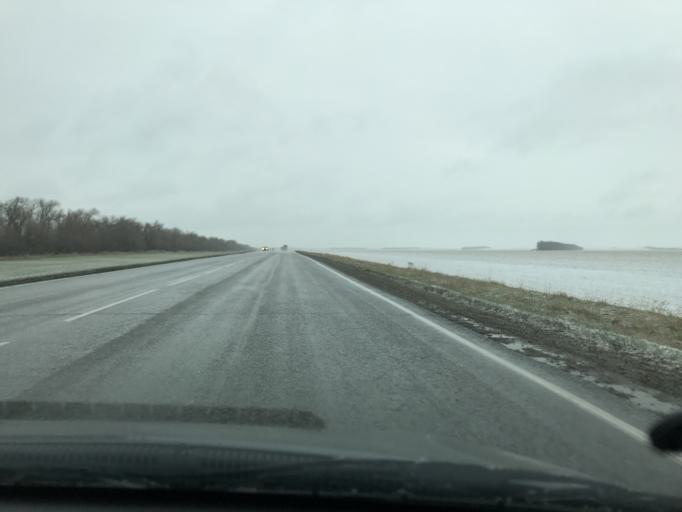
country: RU
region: Rostov
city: Kagal'nitskaya
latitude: 46.9255
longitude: 40.1004
